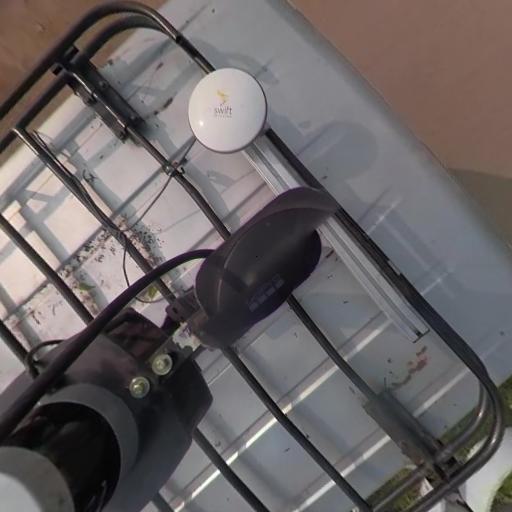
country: IN
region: Telangana
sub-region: Nalgonda
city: Suriapet
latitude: 17.1685
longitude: 79.5060
